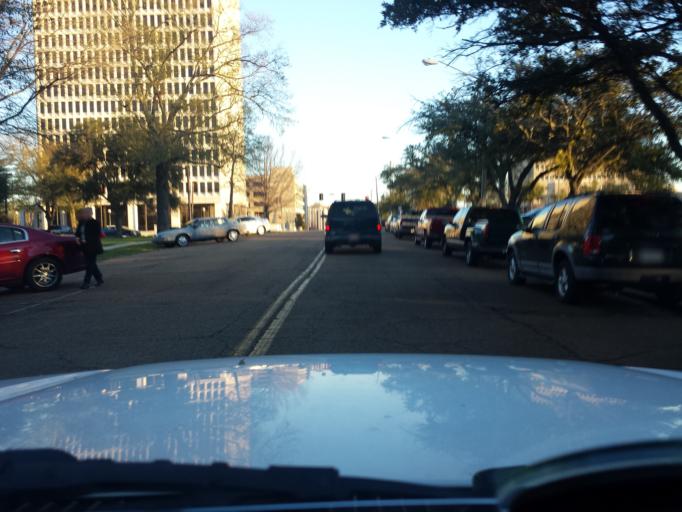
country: US
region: Mississippi
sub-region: Hinds County
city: Jackson
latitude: 32.3038
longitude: -90.1808
